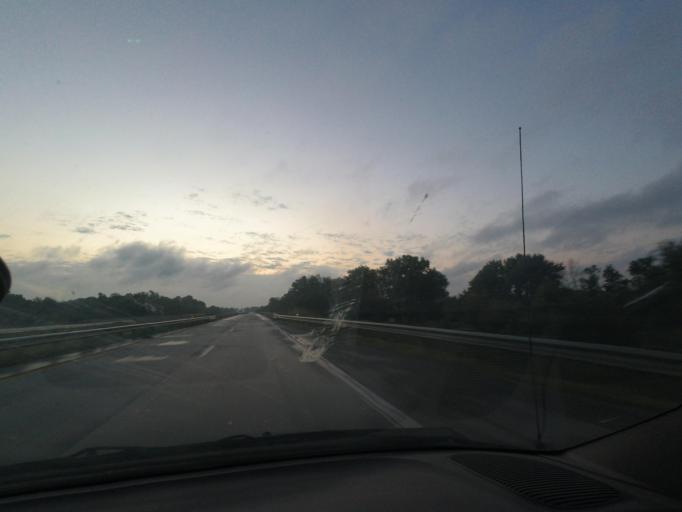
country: US
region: Missouri
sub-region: Linn County
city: Marceline
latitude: 39.7613
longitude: -92.9778
